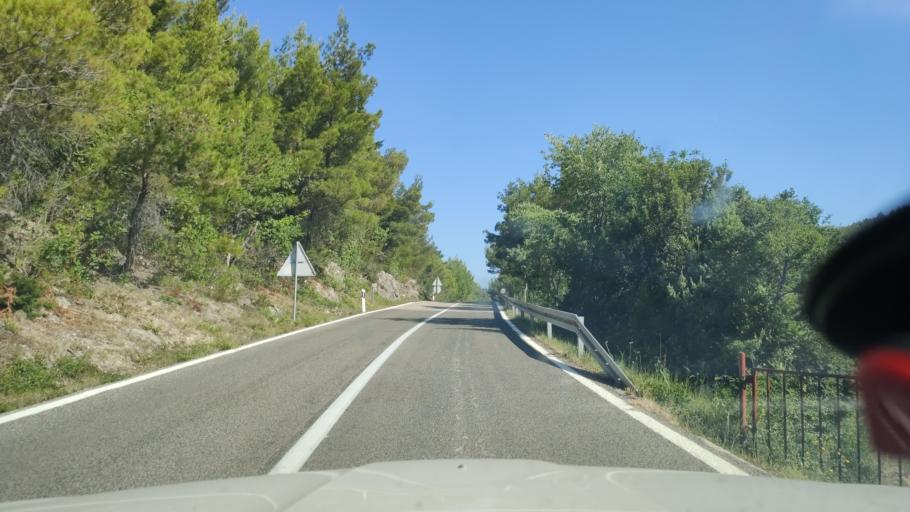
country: HR
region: Sibensko-Kniniska
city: Zaton
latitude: 43.8571
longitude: 15.8947
